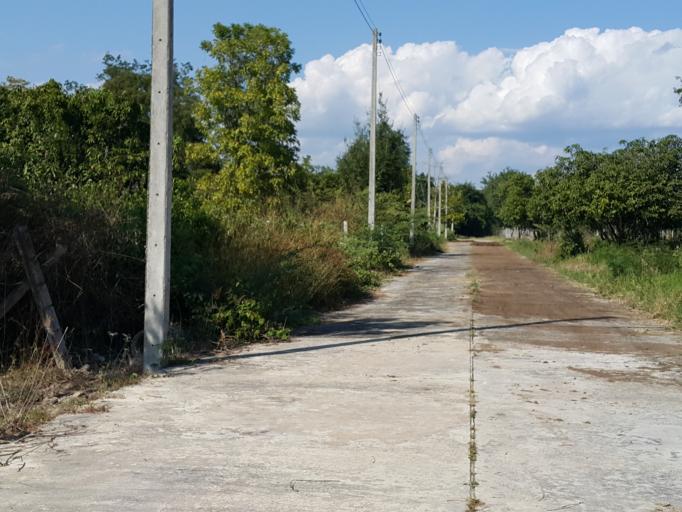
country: TH
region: Chiang Mai
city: San Kamphaeng
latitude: 18.8005
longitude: 99.0974
